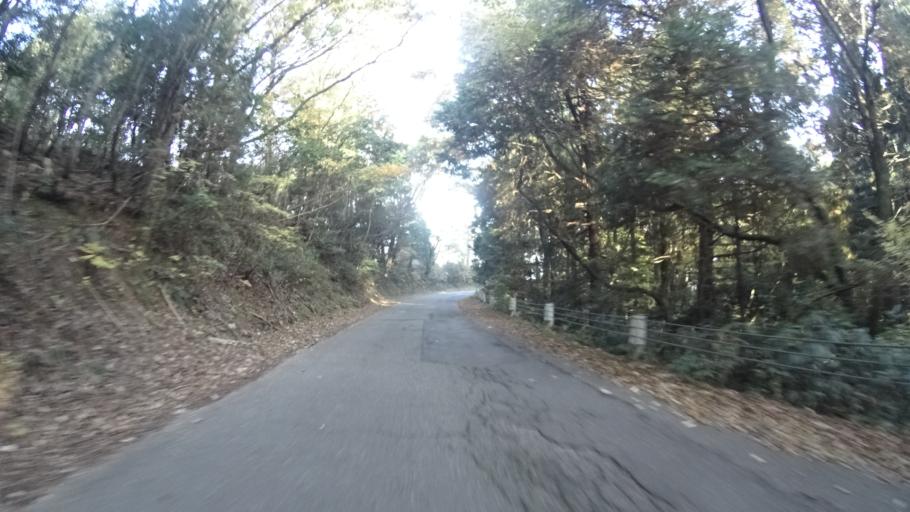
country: JP
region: Ishikawa
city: Nanao
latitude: 37.0213
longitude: 136.9832
